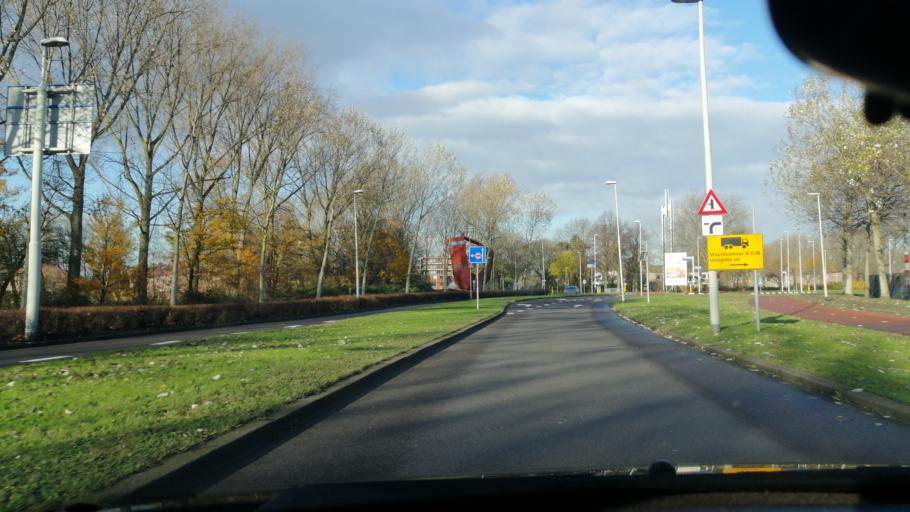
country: NL
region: South Holland
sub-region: Gemeente Albrandswaard
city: Rhoon
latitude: 51.8881
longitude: 4.4250
